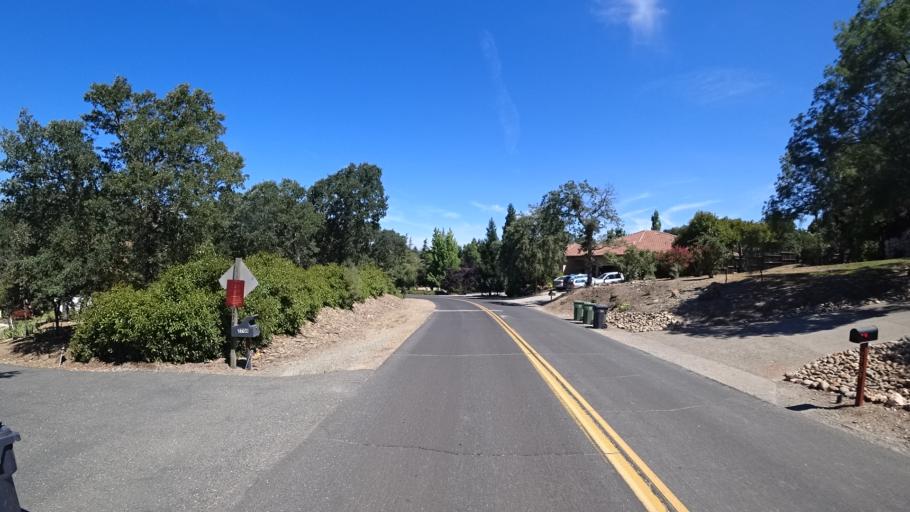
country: US
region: California
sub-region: Calaveras County
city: Valley Springs
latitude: 38.1598
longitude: -120.8332
